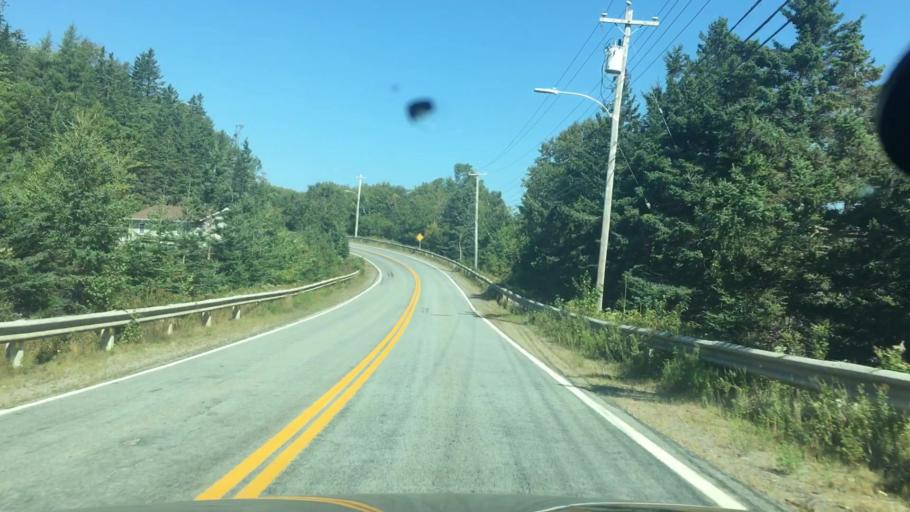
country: CA
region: Nova Scotia
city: New Glasgow
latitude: 44.9160
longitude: -62.5387
